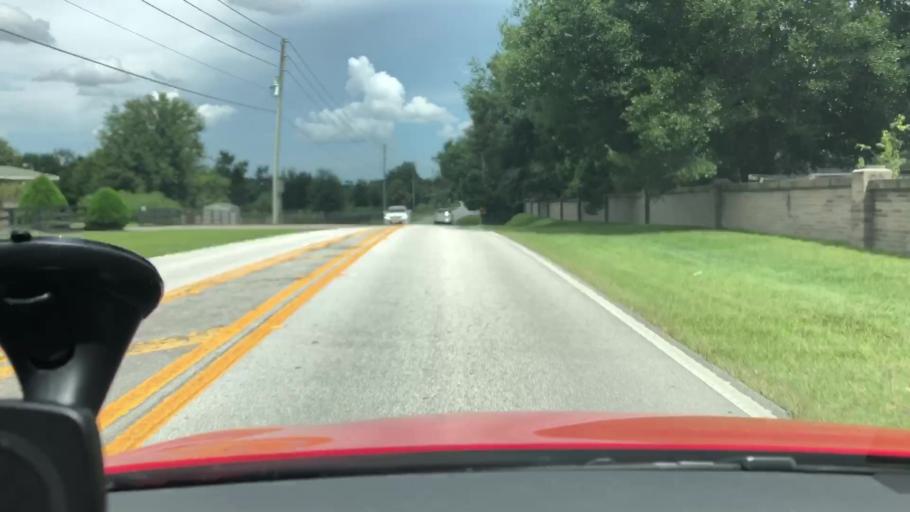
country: US
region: Florida
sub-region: Lake County
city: Mount Dora
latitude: 28.8330
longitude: -81.6515
